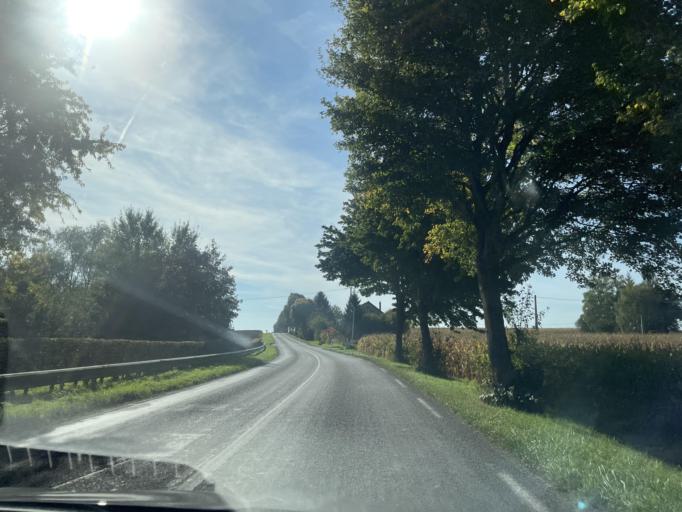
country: FR
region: Ile-de-France
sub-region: Departement de Seine-et-Marne
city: Coulommiers
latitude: 48.8421
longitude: 3.0878
